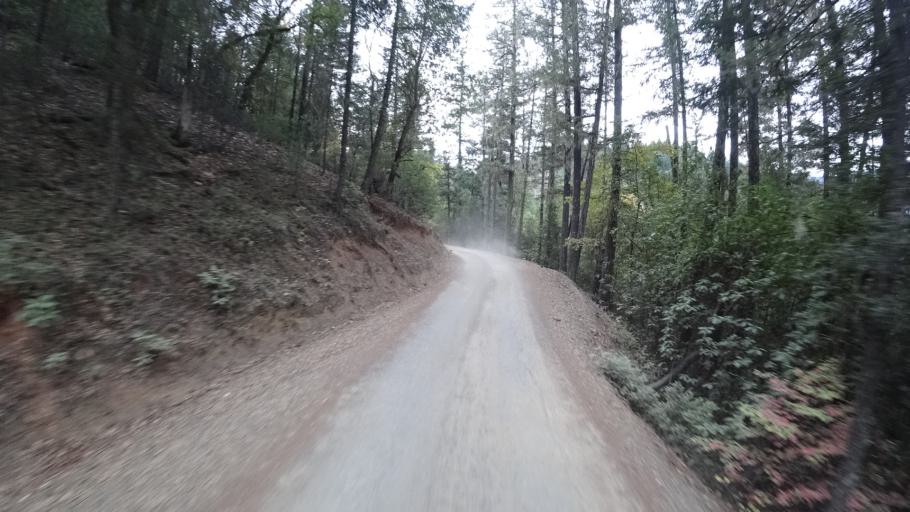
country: US
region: California
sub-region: Siskiyou County
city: Happy Camp
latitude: 41.7840
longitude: -123.3338
